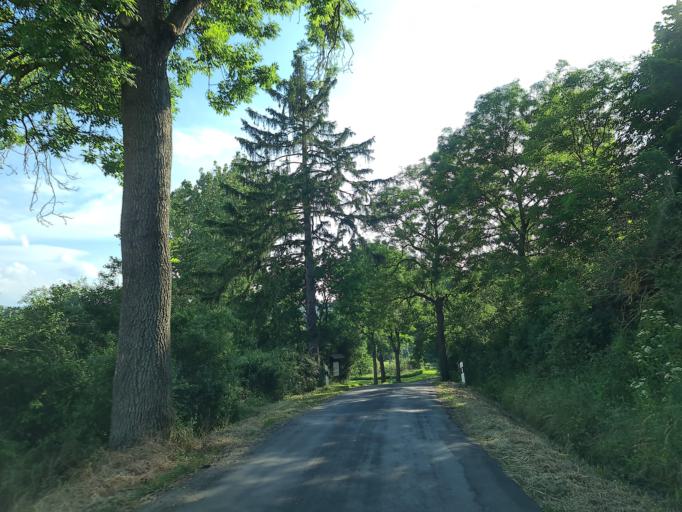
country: DE
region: Saxony
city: Bosenbrunn
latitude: 50.4164
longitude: 12.0985
